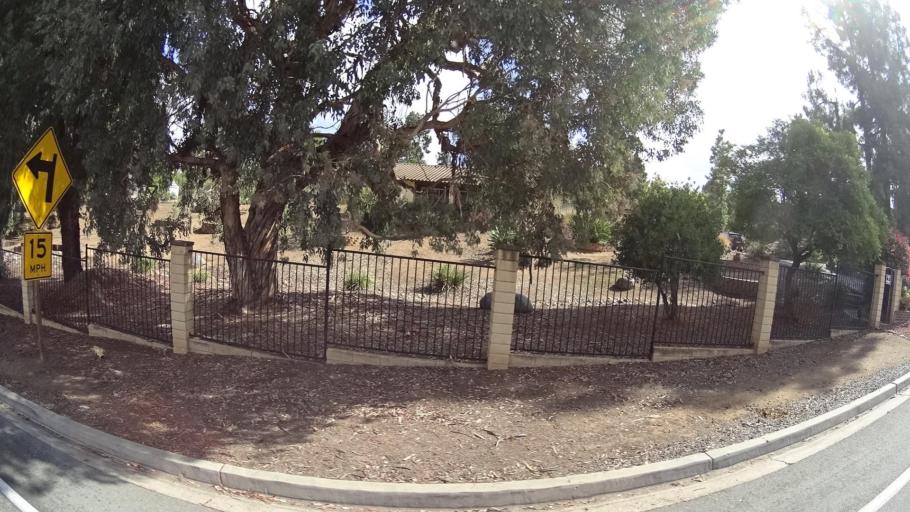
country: US
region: California
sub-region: San Diego County
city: Granite Hills
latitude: 32.7799
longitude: -116.9026
